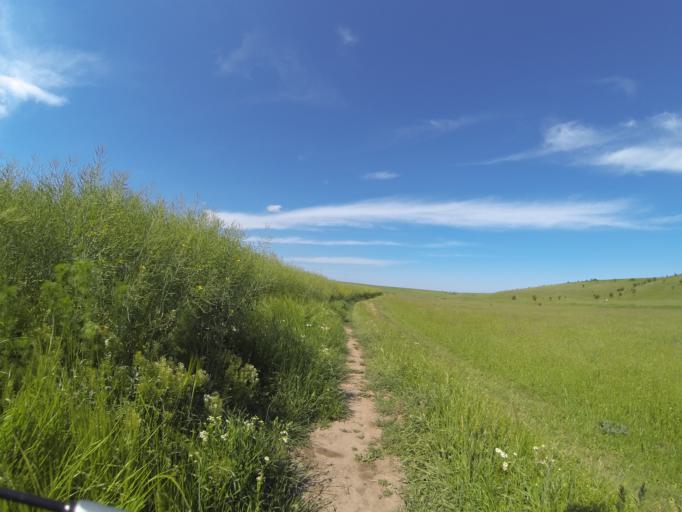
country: RO
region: Dolj
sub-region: Comuna Leu
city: Leu
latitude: 44.2505
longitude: 24.0126
